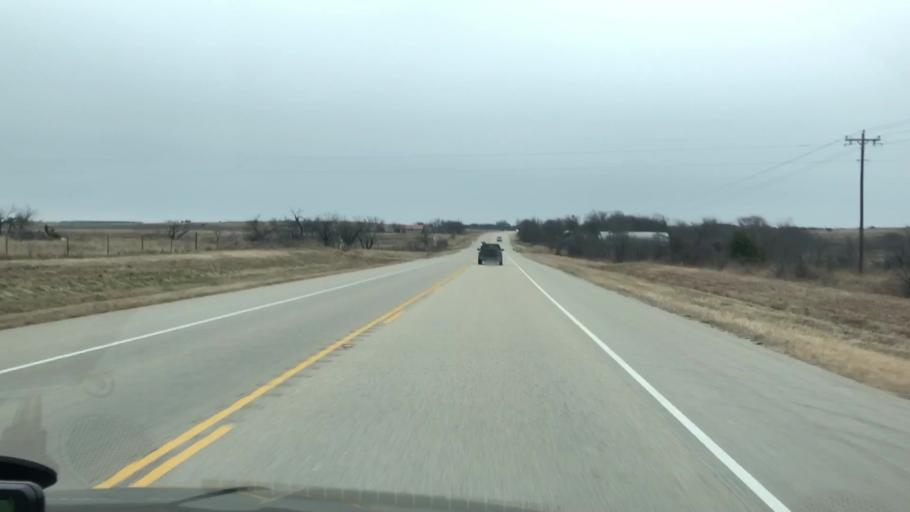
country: US
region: Texas
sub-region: Hamilton County
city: Hamilton
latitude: 31.6416
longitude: -98.1492
